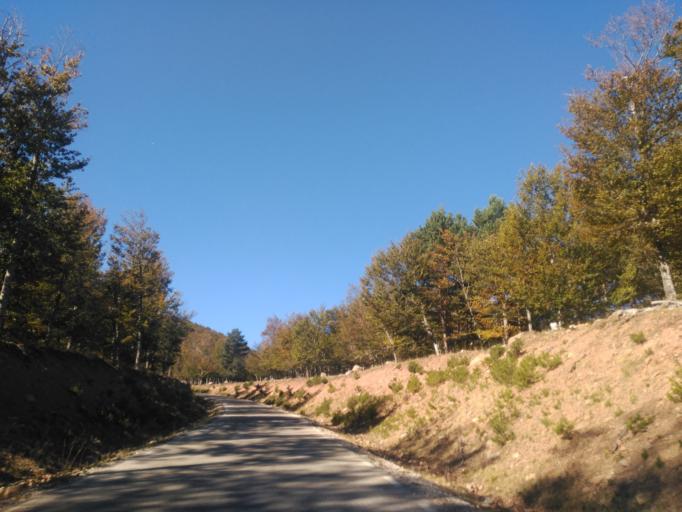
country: ES
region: La Rioja
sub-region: Provincia de La Rioja
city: Viniegra de Arriba
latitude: 42.0160
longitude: -2.8214
